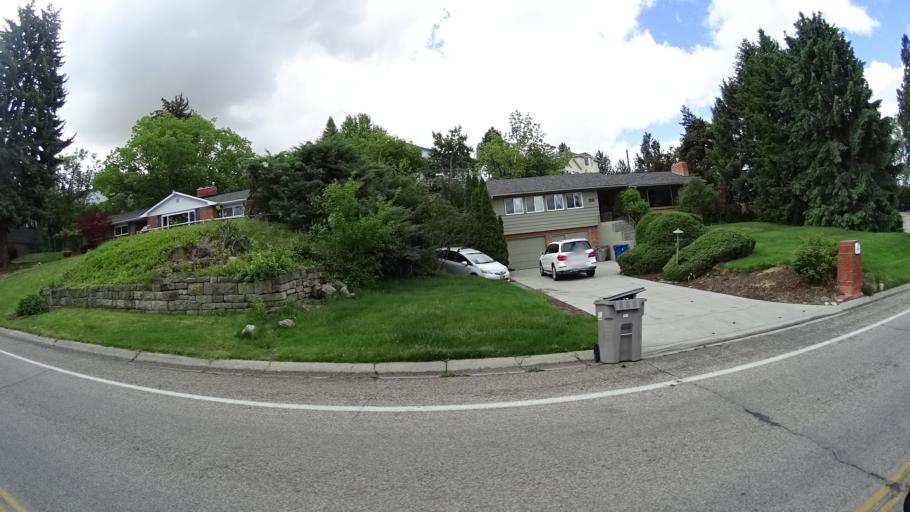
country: US
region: Idaho
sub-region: Ada County
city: Boise
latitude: 43.6449
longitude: -116.2000
